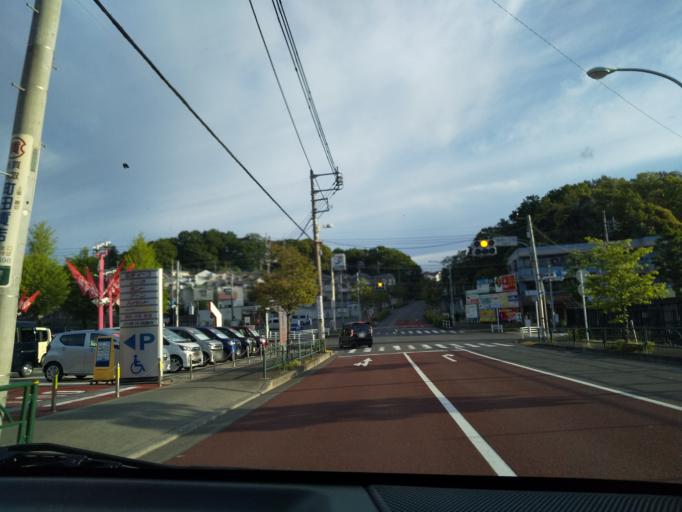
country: JP
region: Tokyo
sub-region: Machida-shi
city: Machida
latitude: 35.5713
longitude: 139.4544
